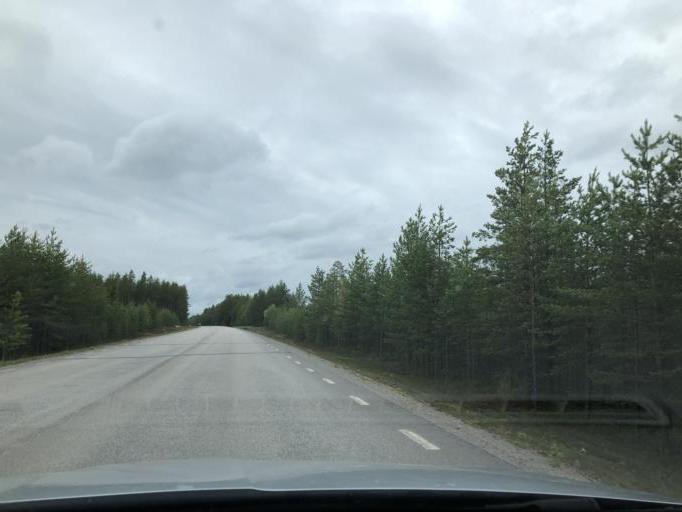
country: SE
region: Norrbotten
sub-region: Pitea Kommun
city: Bergsviken
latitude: 65.3738
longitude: 21.3516
